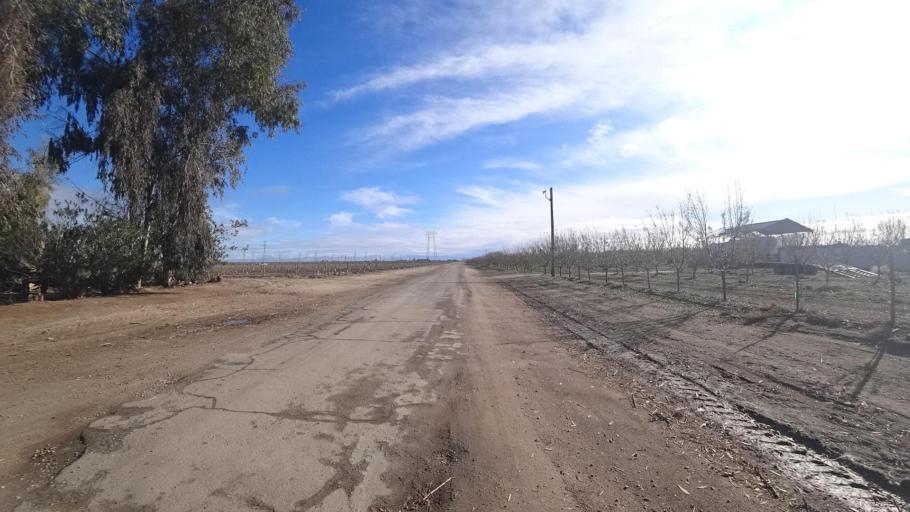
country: US
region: California
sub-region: Kern County
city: Shafter
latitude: 35.3835
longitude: -119.2776
